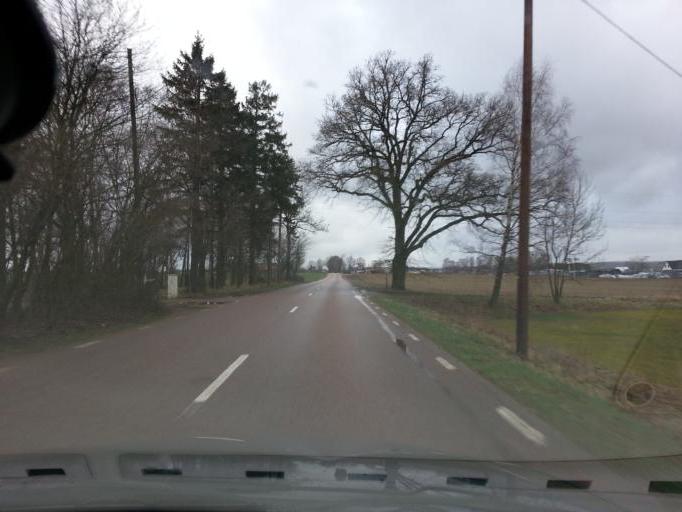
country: SE
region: Skane
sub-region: Astorps Kommun
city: Kvidinge
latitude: 56.1161
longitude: 13.0830
